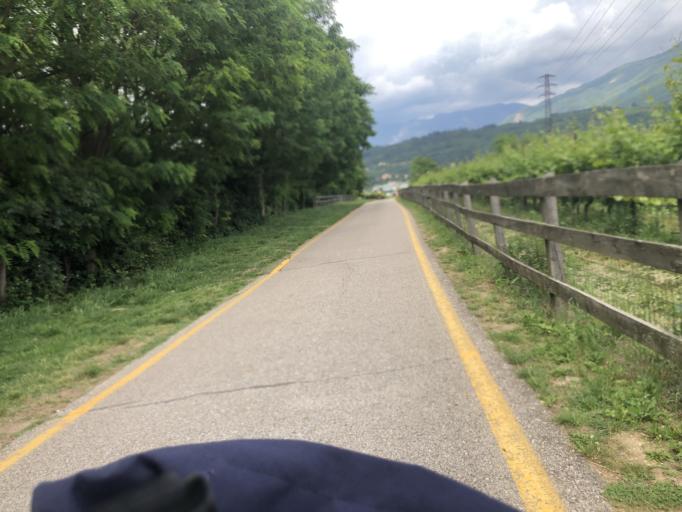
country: IT
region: Trentino-Alto Adige
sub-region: Provincia di Trento
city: Nogaredo
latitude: 45.8981
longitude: 11.0260
